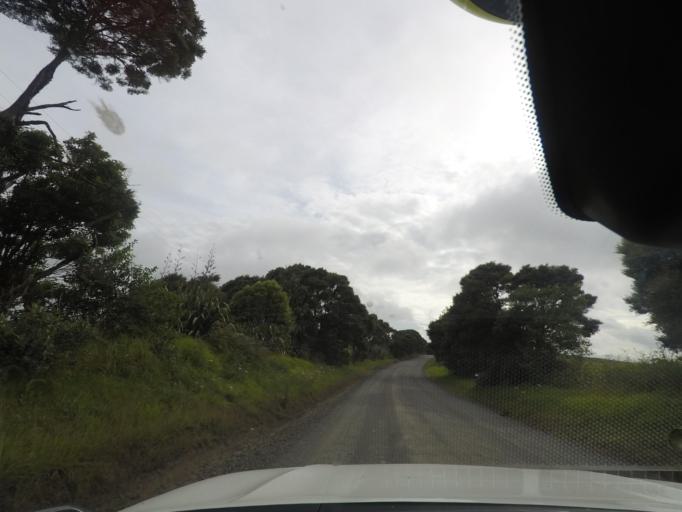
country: NZ
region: Auckland
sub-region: Auckland
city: Parakai
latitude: -36.4855
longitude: 174.2487
